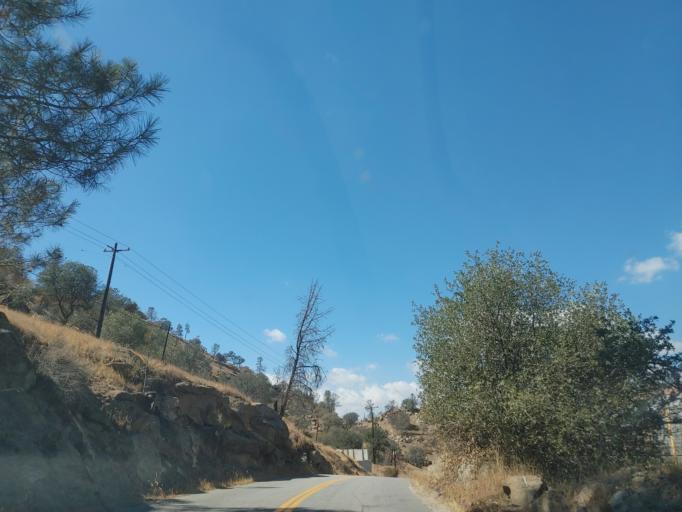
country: US
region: California
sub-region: Kern County
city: Bear Valley Springs
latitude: 35.2180
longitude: -118.5570
